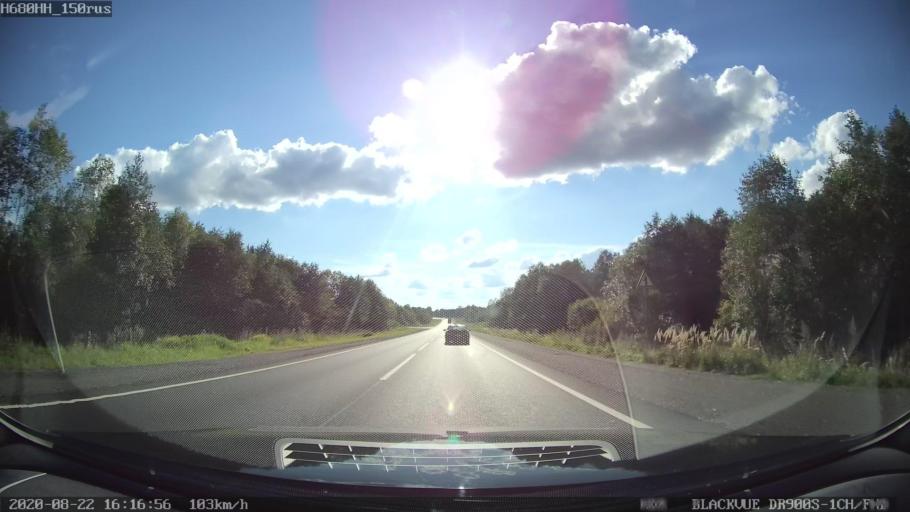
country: RU
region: Tverskaya
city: Rameshki
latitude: 57.4299
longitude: 36.1680
